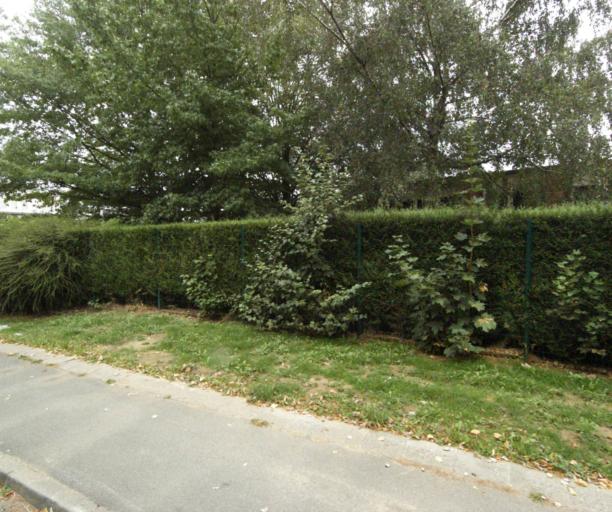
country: FR
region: Nord-Pas-de-Calais
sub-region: Departement du Nord
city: Mons-en-Baroeul
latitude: 50.6477
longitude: 3.1282
